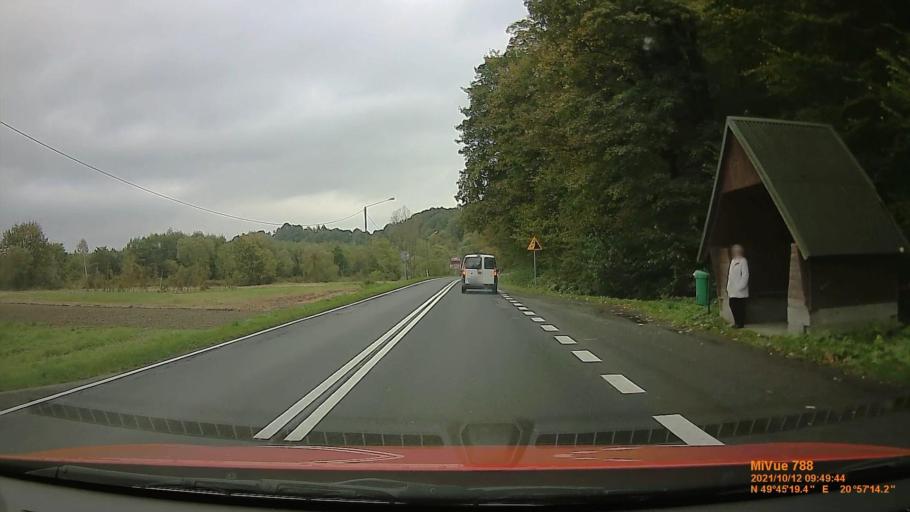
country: PL
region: Lesser Poland Voivodeship
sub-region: Powiat tarnowski
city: Ciezkowice
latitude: 49.7554
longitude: 20.9541
